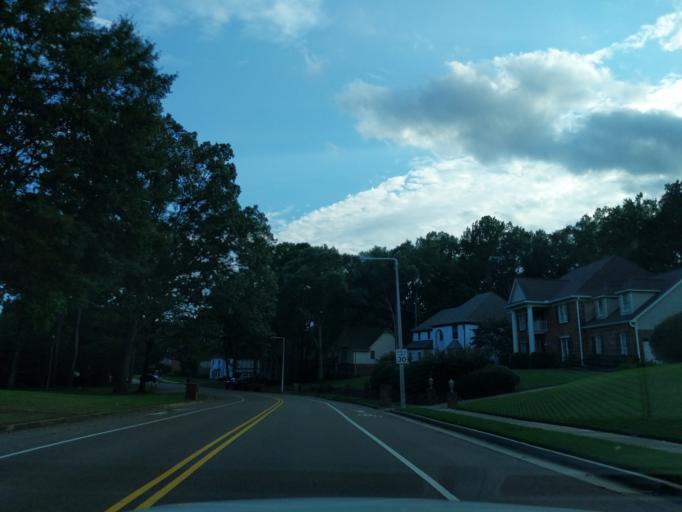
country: US
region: Tennessee
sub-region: Shelby County
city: Germantown
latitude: 35.0699
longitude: -89.7779
